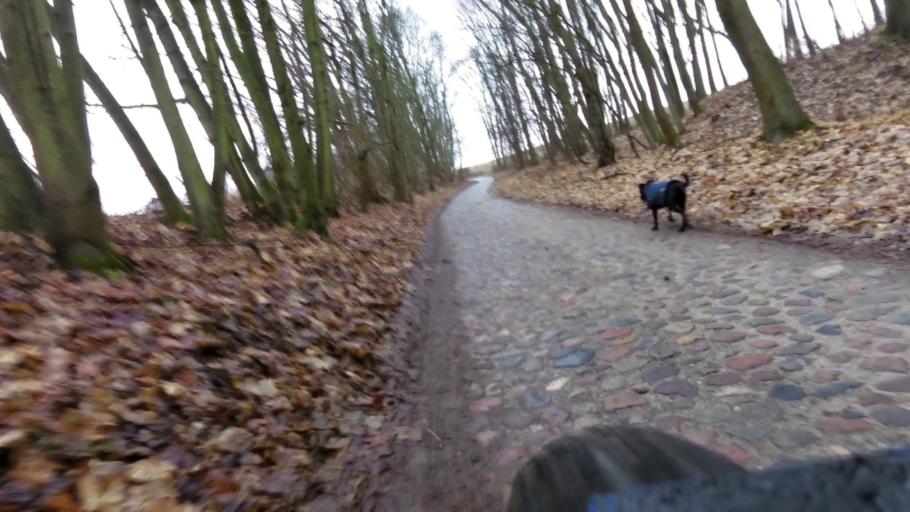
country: PL
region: Lubusz
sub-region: Powiat gorzowski
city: Kostrzyn nad Odra
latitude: 52.6223
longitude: 14.7006
